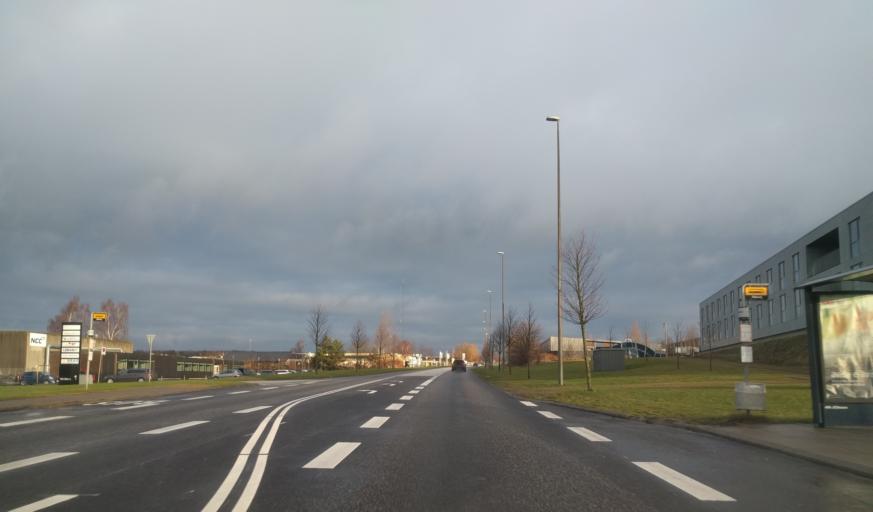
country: DK
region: North Denmark
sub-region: Alborg Kommune
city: Gistrup
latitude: 57.0233
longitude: 9.9757
